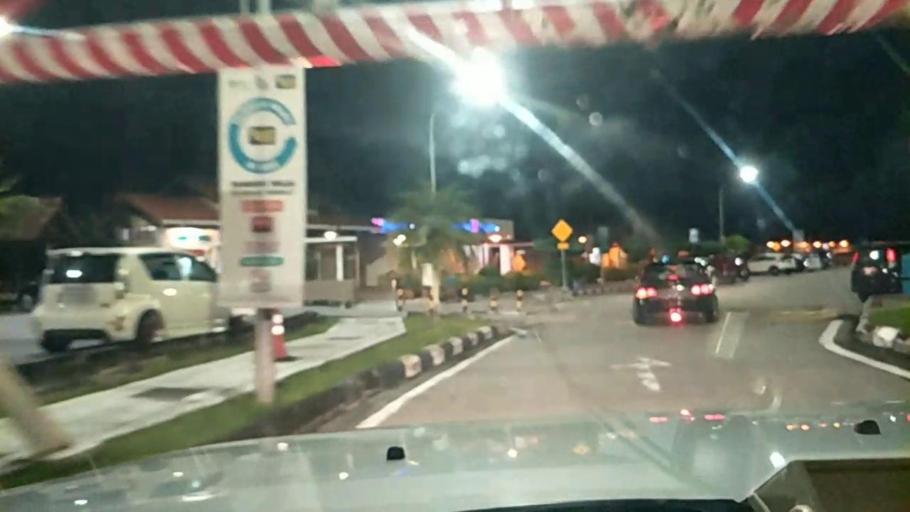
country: MY
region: Perak
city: Bidur
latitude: 4.0436
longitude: 101.3109
